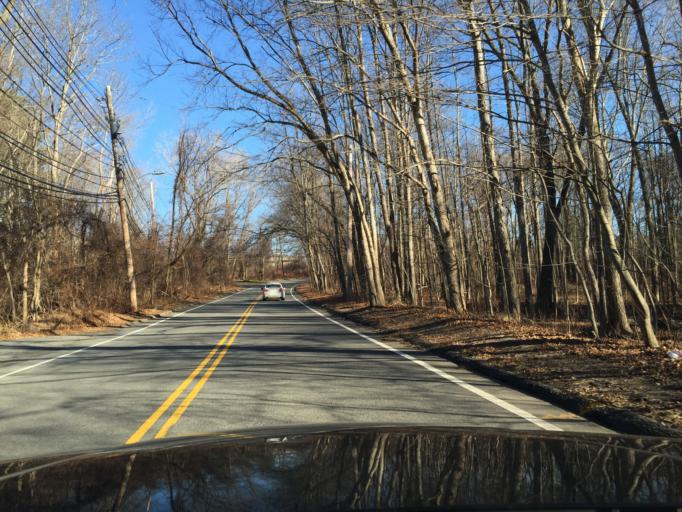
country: US
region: Massachusetts
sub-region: Middlesex County
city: Burlington
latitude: 42.4788
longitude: -71.2018
